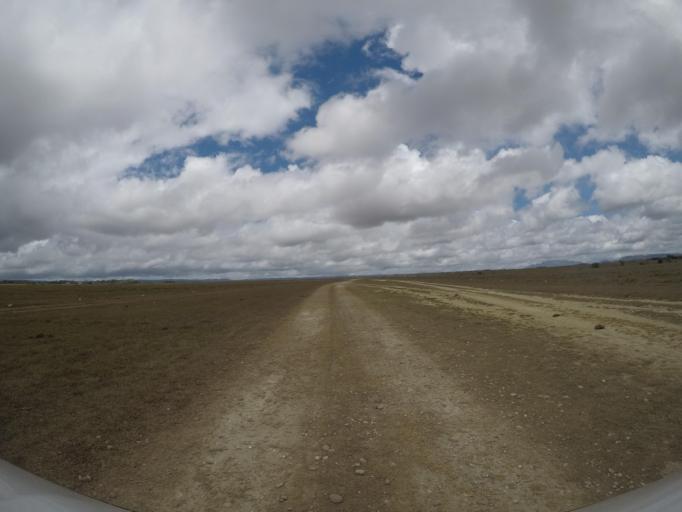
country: TL
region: Lautem
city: Lospalos
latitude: -8.4441
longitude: 126.9892
